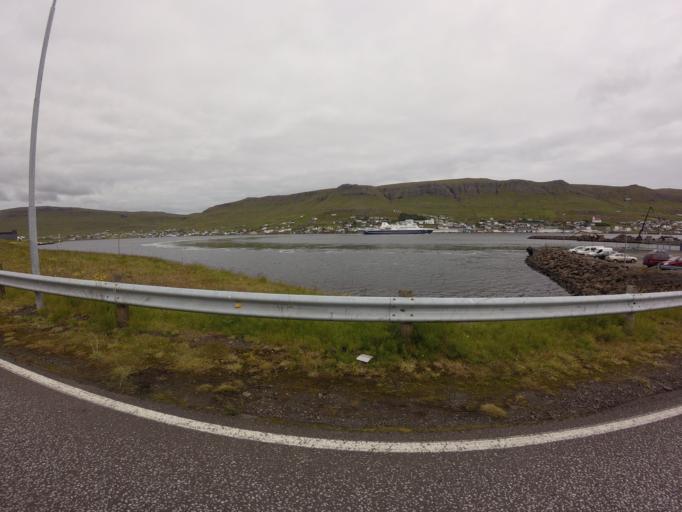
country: FO
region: Suduroy
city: Tvoroyri
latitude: 61.5483
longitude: -6.8204
